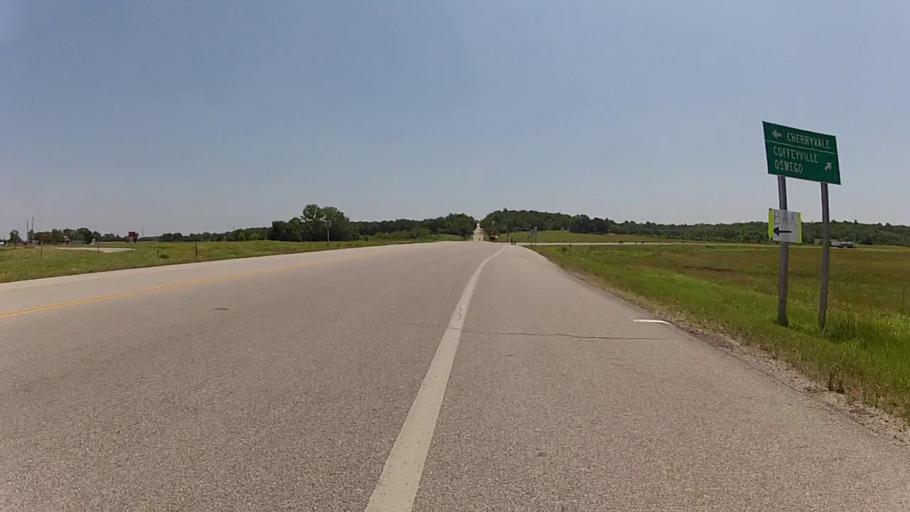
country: US
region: Kansas
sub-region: Montgomery County
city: Cherryvale
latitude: 37.2238
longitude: -95.5876
